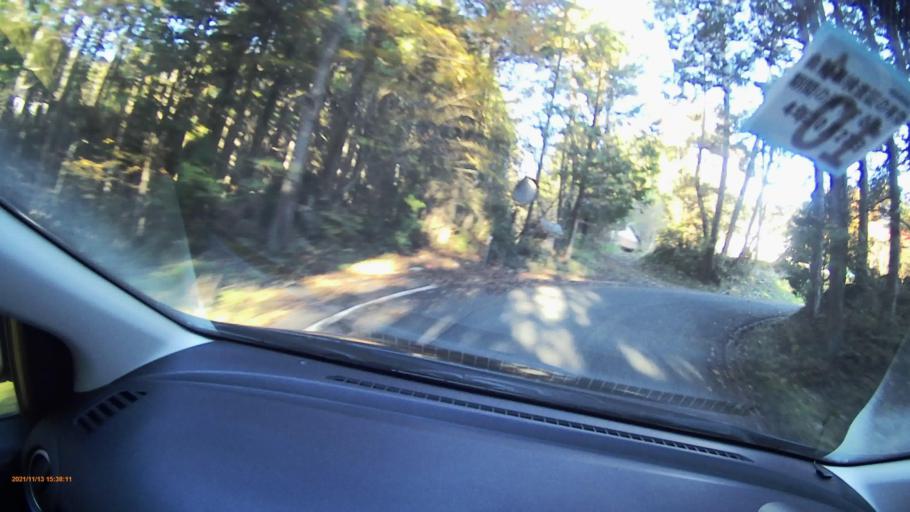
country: JP
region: Gifu
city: Nakatsugawa
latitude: 35.5828
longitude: 137.3793
